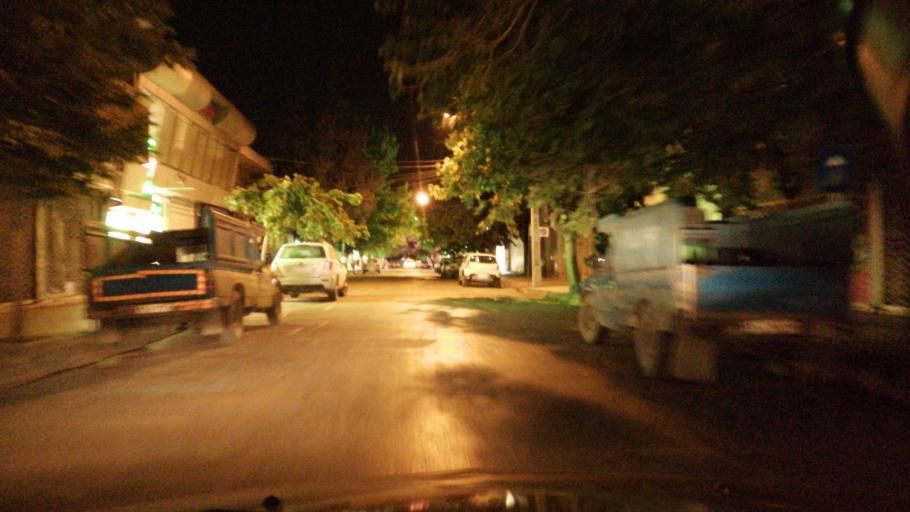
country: IR
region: Razavi Khorasan
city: Mashhad
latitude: 36.3071
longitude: 59.6000
